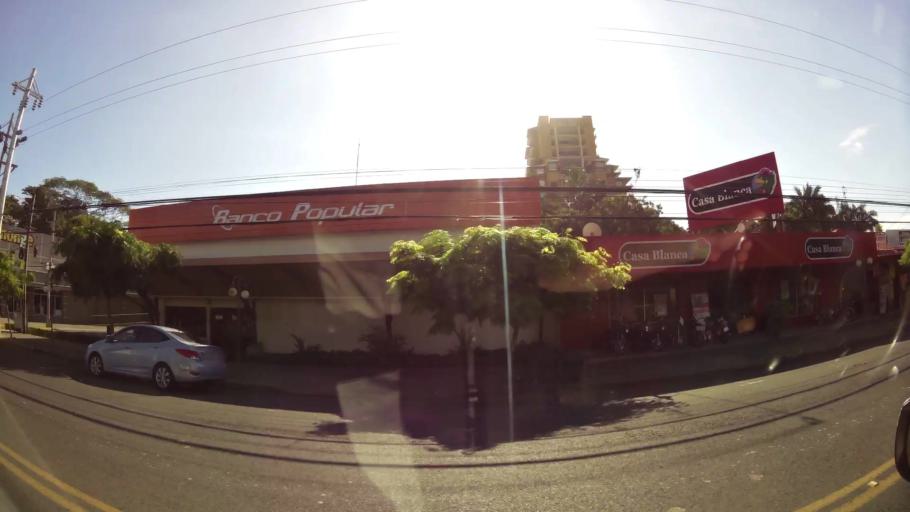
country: CR
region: Puntarenas
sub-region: Canton de Garabito
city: Jaco
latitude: 9.6118
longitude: -84.6258
